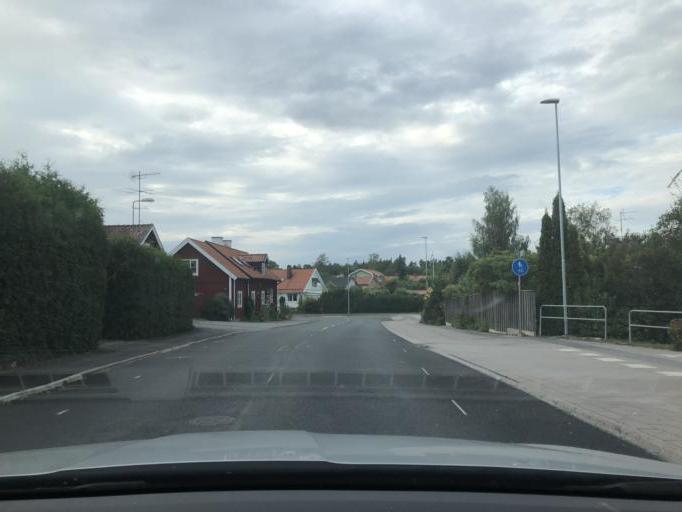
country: SE
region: Soedermanland
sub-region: Strangnas Kommun
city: Mariefred
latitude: 59.2614
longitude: 17.2239
